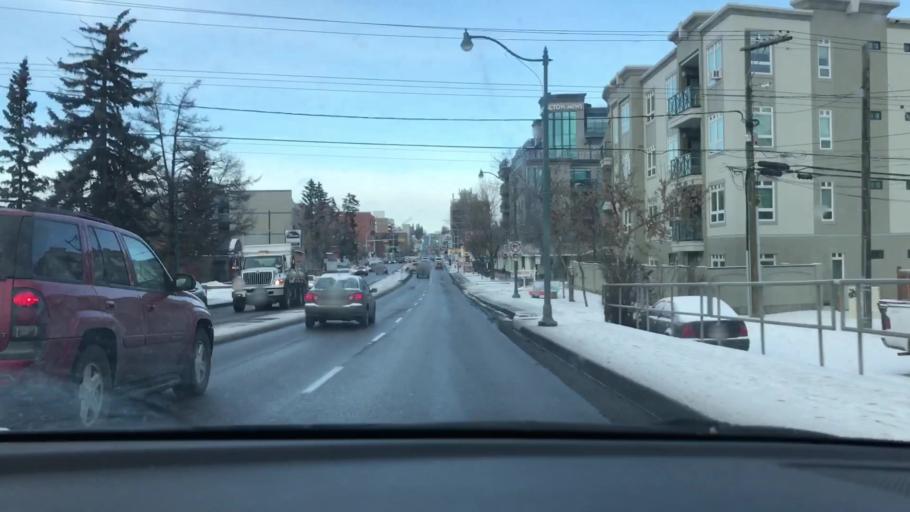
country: CA
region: Alberta
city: Calgary
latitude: 51.0504
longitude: -114.0946
